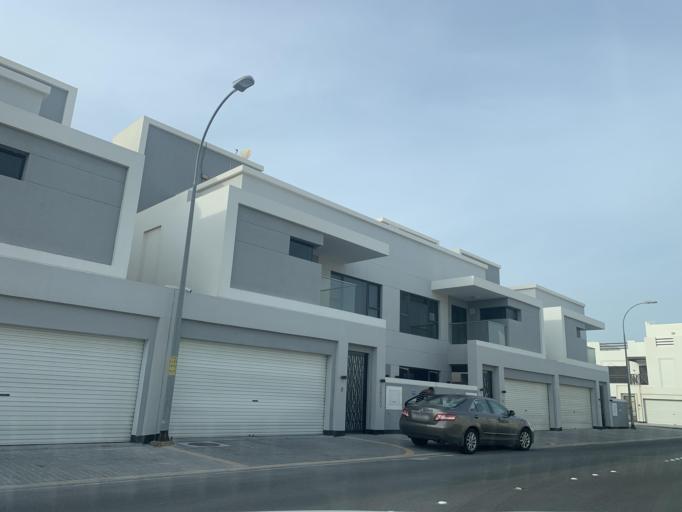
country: BH
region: Muharraq
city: Al Muharraq
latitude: 26.3154
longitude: 50.6285
